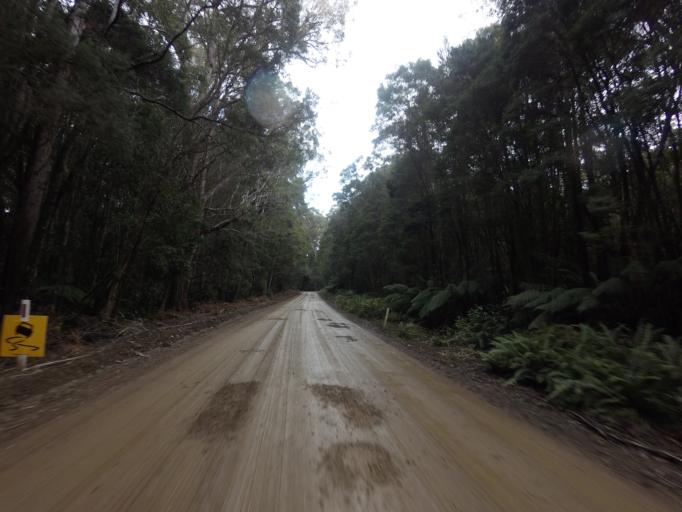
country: AU
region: Tasmania
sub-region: Huon Valley
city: Geeveston
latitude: -43.4020
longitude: 146.8632
